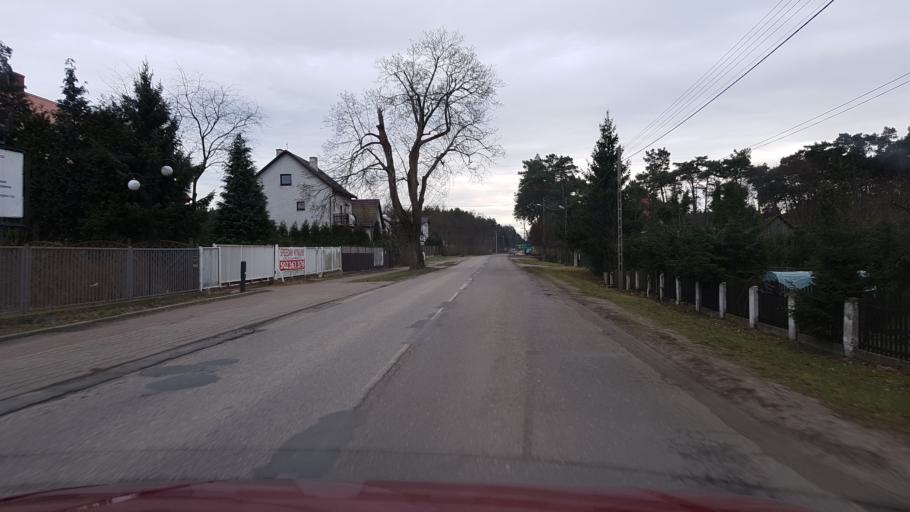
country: PL
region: West Pomeranian Voivodeship
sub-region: Powiat policki
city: Dobra
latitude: 53.5365
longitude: 14.4670
